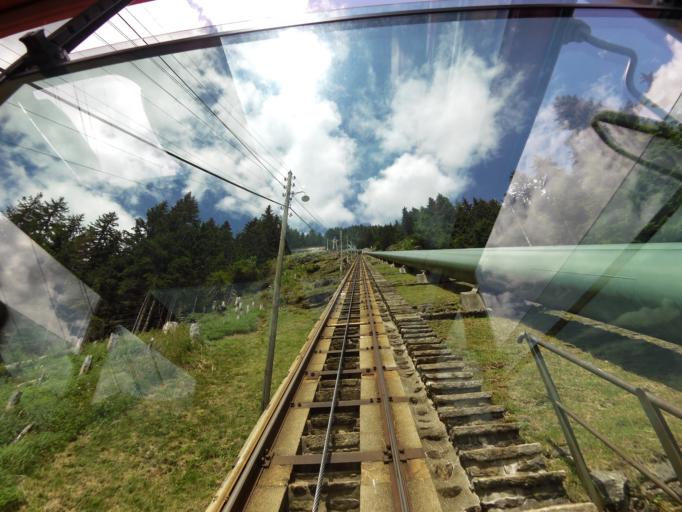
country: CH
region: Ticino
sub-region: Leventina District
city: Airolo
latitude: 46.5260
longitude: 8.6730
